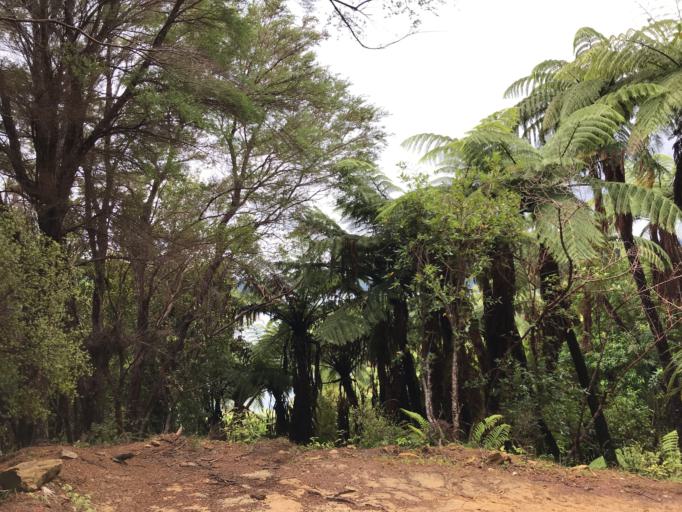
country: NZ
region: Marlborough
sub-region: Marlborough District
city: Picton
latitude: -41.1148
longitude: 174.1637
